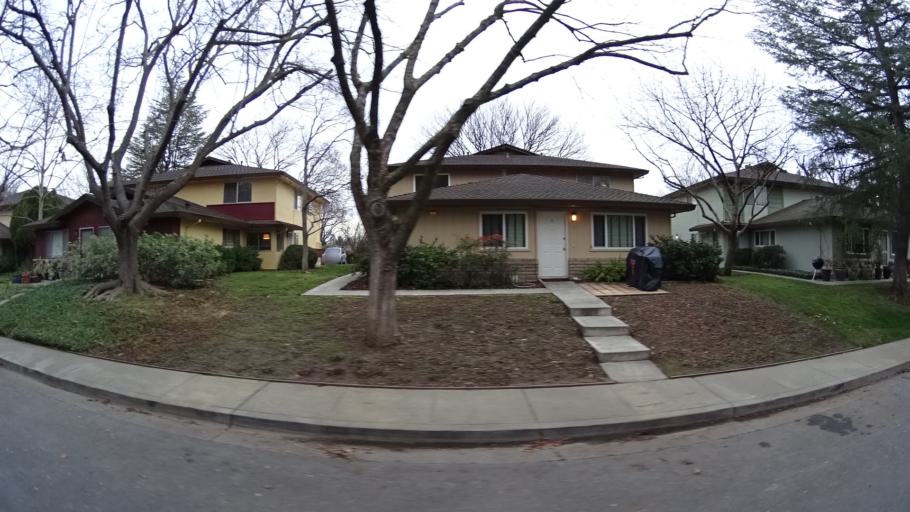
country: US
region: California
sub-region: Yolo County
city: Davis
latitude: 38.5677
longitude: -121.7284
